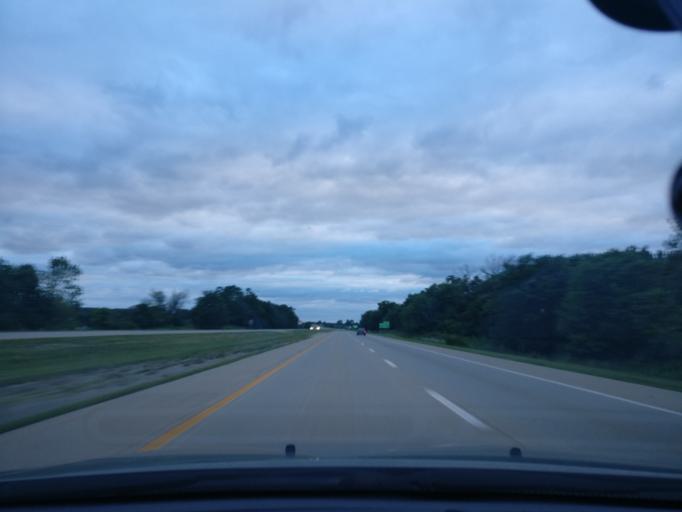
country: US
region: Ohio
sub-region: Greene County
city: Wilberforce
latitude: 39.6894
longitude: -83.8678
